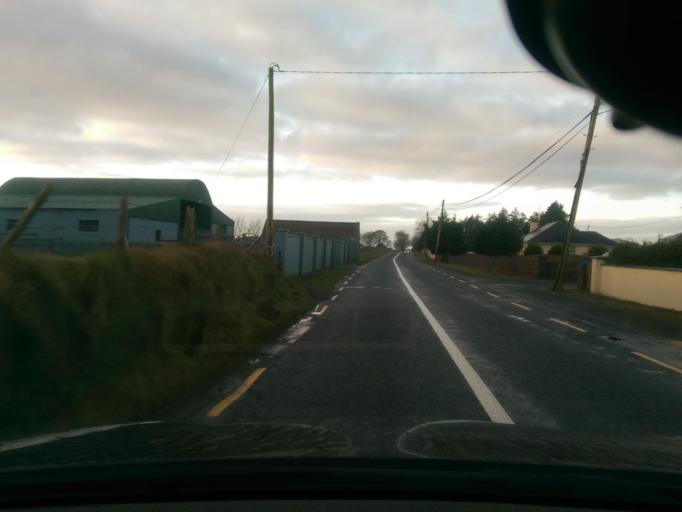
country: IE
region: Connaught
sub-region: County Galway
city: Athenry
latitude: 53.4219
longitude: -8.6029
